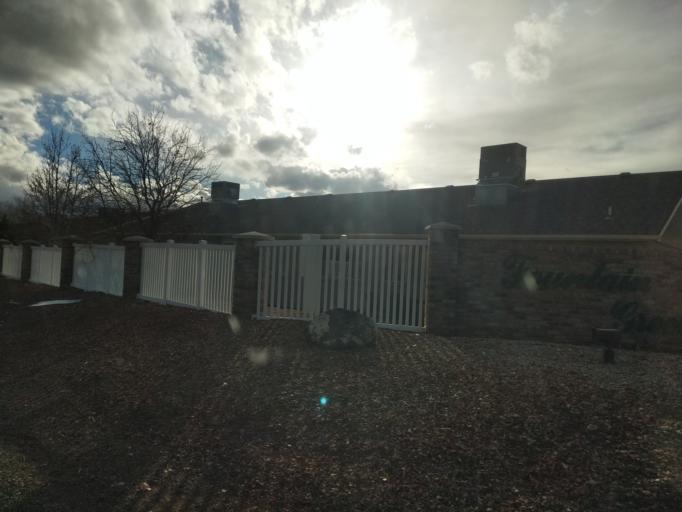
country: US
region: Colorado
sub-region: Mesa County
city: Redlands
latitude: 39.1095
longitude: -108.5896
